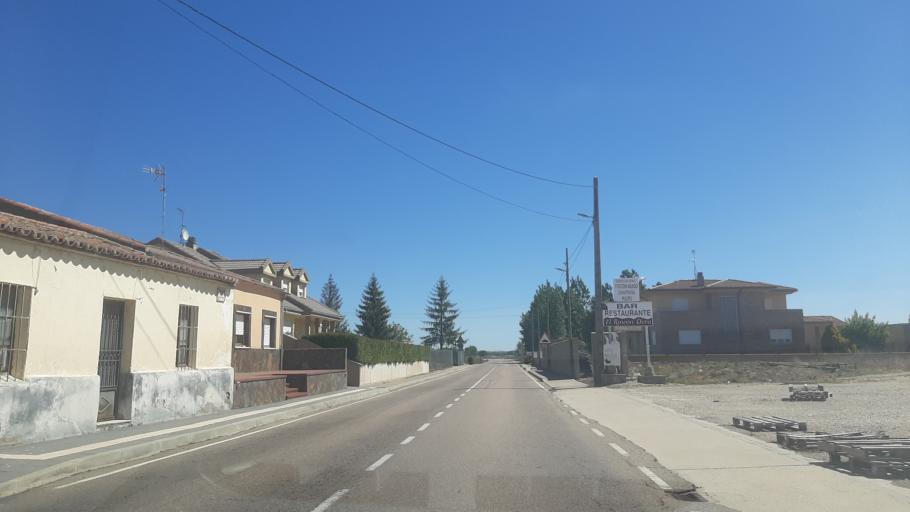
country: ES
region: Castille and Leon
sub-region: Provincia de Salamanca
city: Galisancho
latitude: 40.7422
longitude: -5.5767
